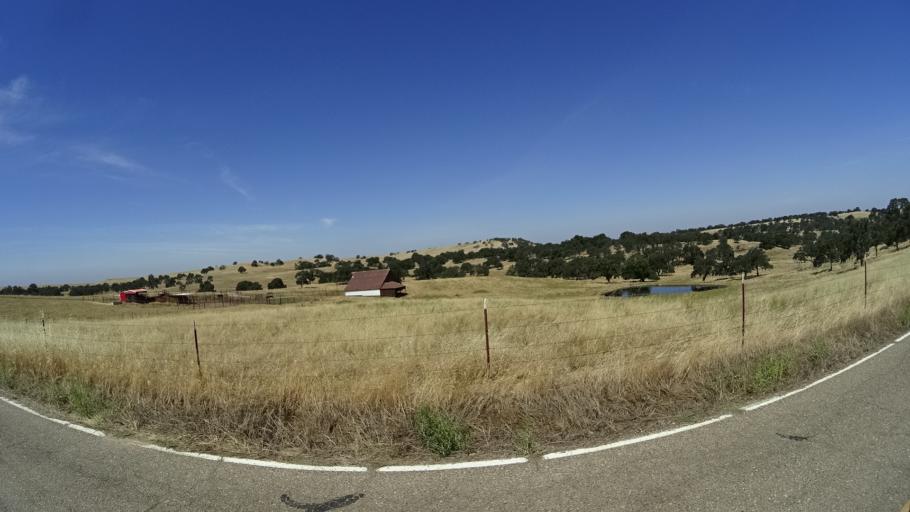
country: US
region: California
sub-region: Calaveras County
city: Rancho Calaveras
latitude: 38.1526
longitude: -120.9540
